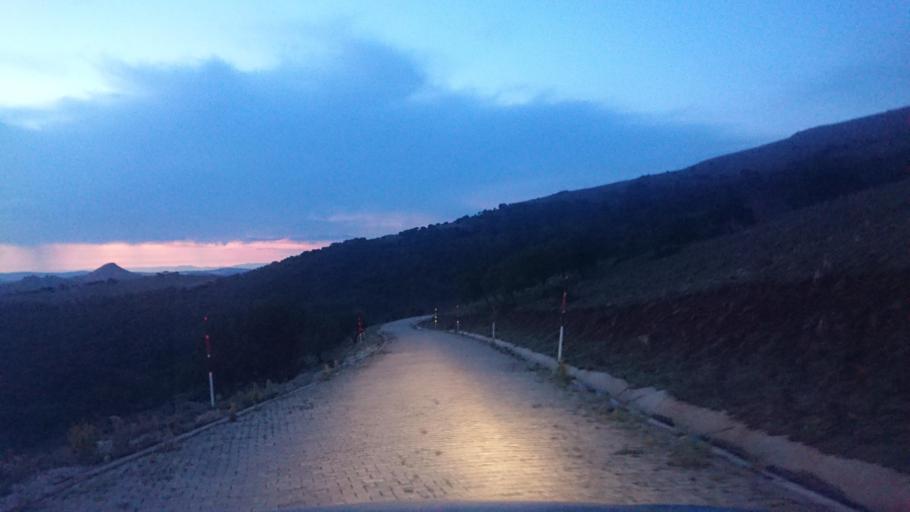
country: TR
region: Aksaray
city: Ortakoy
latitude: 38.6412
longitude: 34.0248
